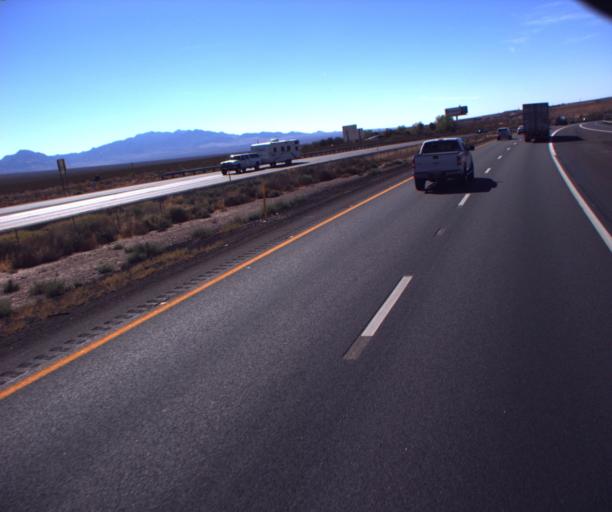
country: US
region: Arizona
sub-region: Mohave County
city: Beaver Dam
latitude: 36.8958
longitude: -113.9110
